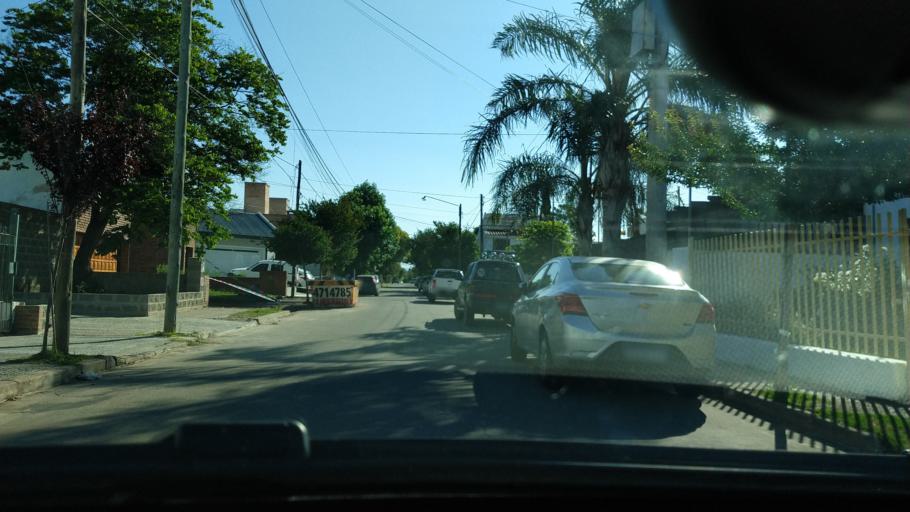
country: AR
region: Cordoba
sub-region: Departamento de Capital
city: Cordoba
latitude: -31.3652
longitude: -64.2291
